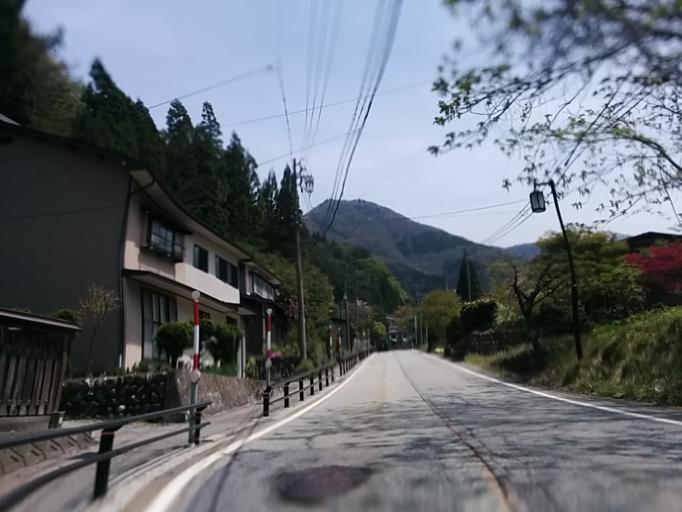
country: JP
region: Gifu
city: Takayama
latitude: 36.2424
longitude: 137.5218
